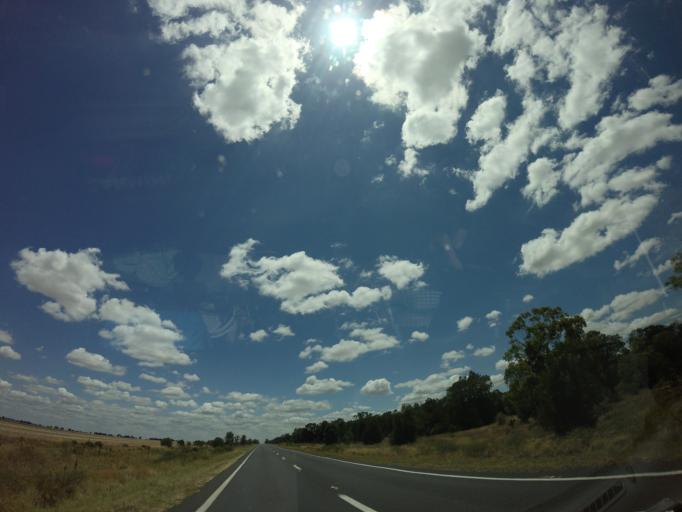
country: AU
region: New South Wales
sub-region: Moree Plains
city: Boggabilla
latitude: -28.8224
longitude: 150.2341
